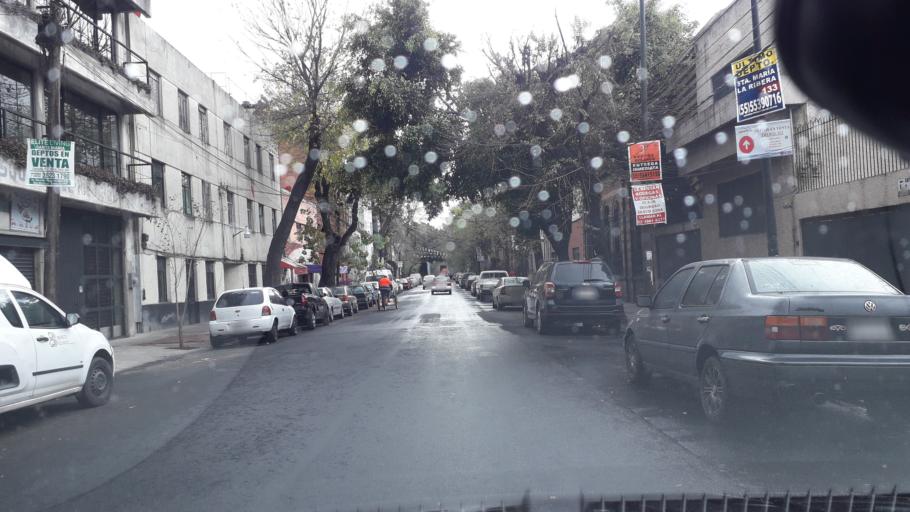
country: MX
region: Mexico City
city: Cuauhtemoc
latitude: 19.4541
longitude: -99.1553
